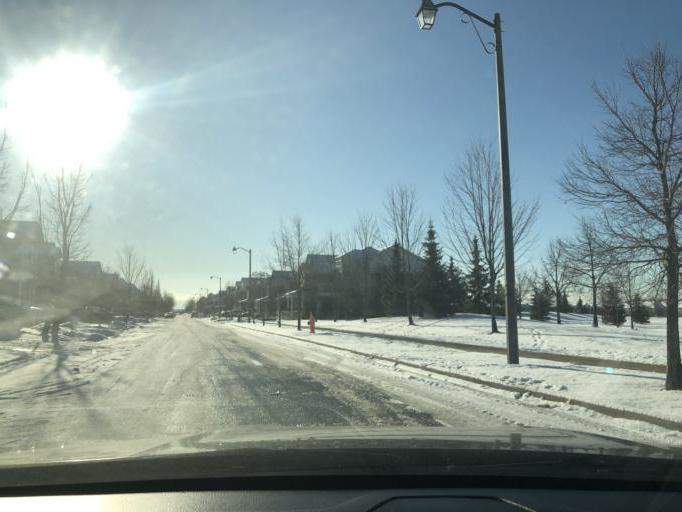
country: CA
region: Ontario
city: Scarborough
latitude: 43.7787
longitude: -79.1378
